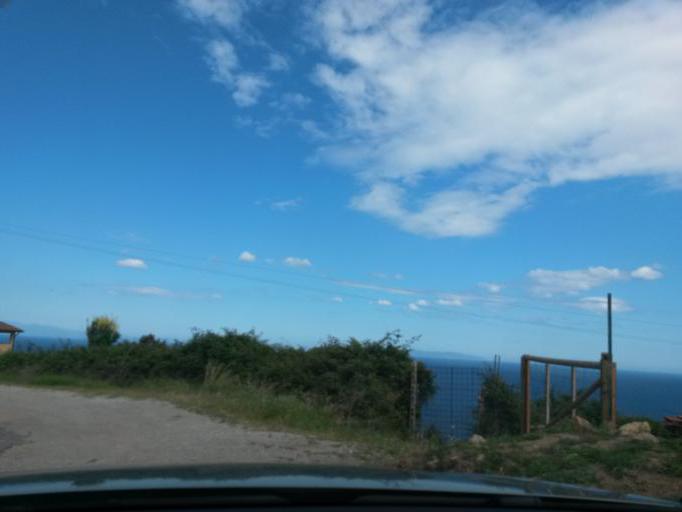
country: IT
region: Tuscany
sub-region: Provincia di Livorno
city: Marciana
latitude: 42.8035
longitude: 10.1520
